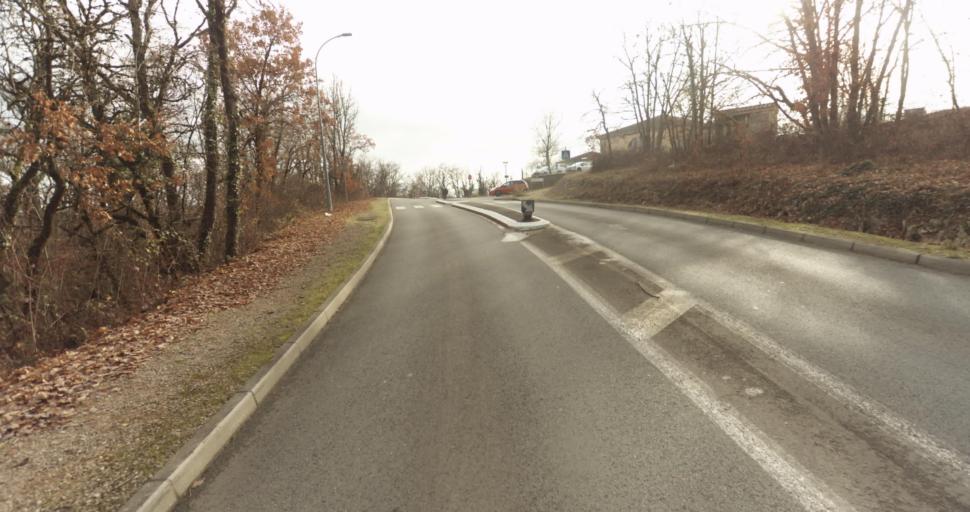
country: FR
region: Midi-Pyrenees
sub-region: Departement du Lot
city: Figeac
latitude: 44.6114
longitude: 2.0117
